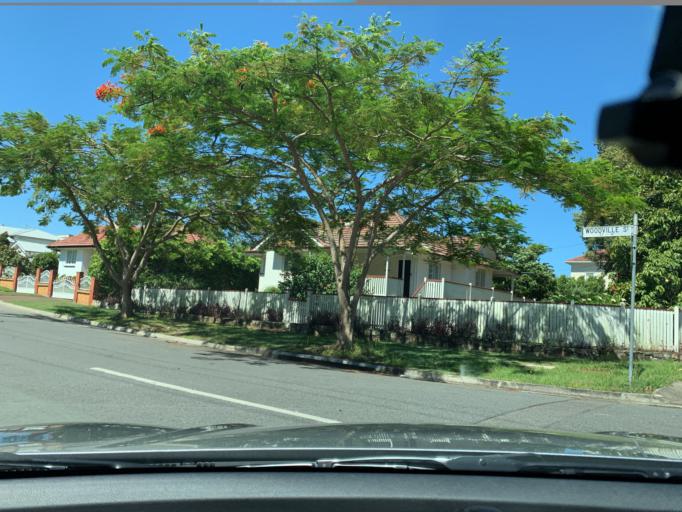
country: AU
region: Queensland
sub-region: Brisbane
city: Ascot
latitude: -27.4194
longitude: 153.0648
